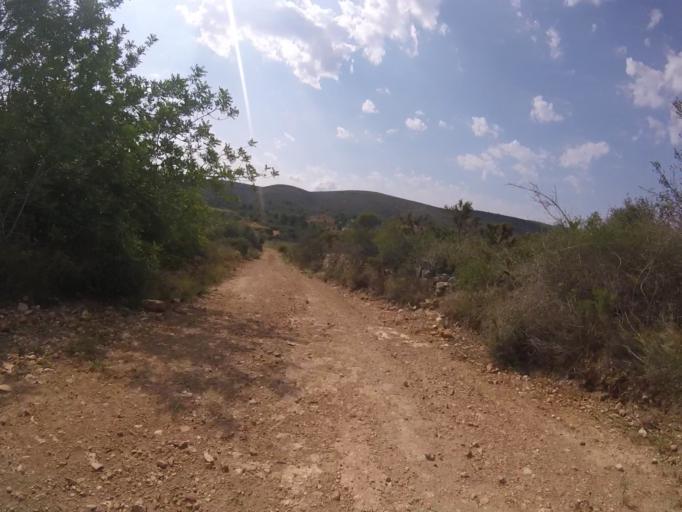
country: ES
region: Valencia
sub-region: Provincia de Castello
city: Alcala de Xivert
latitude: 40.3371
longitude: 0.1965
